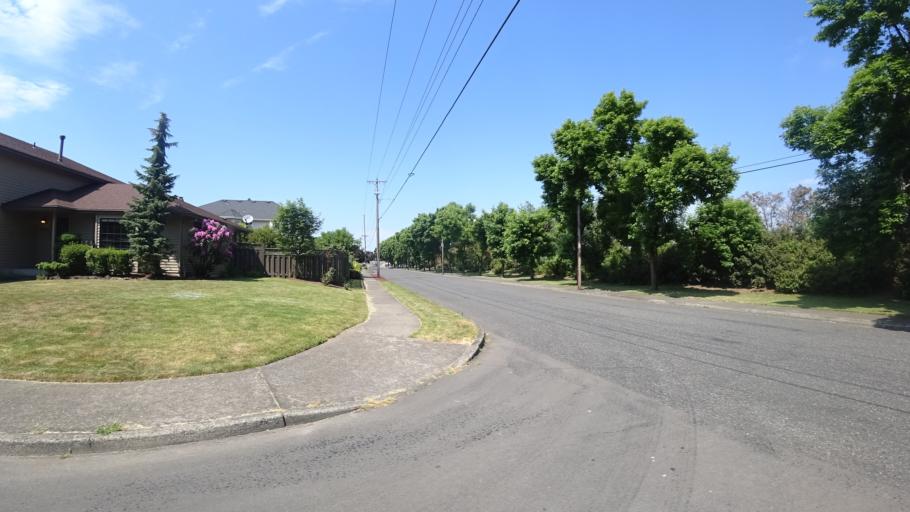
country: US
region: Oregon
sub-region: Multnomah County
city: Fairview
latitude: 45.5383
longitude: -122.4893
